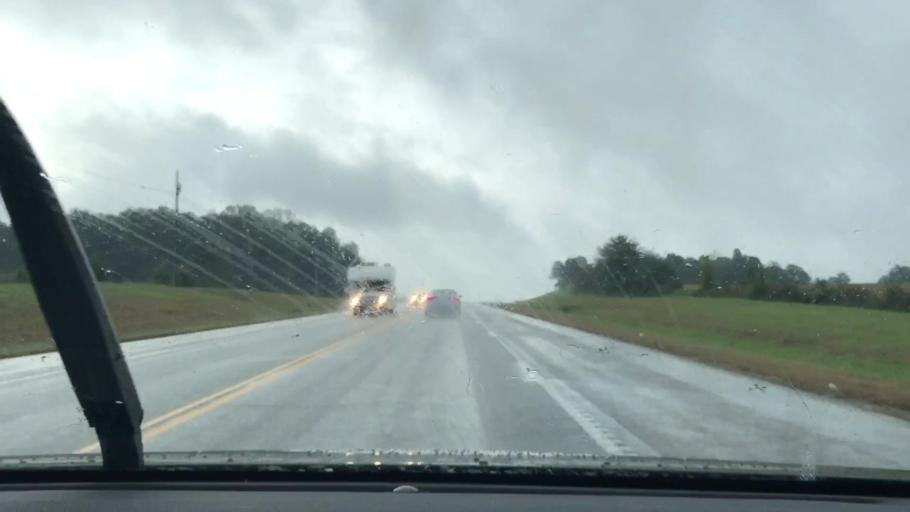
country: US
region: Tennessee
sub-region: Sumner County
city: Westmoreland
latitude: 36.5235
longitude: -86.1490
